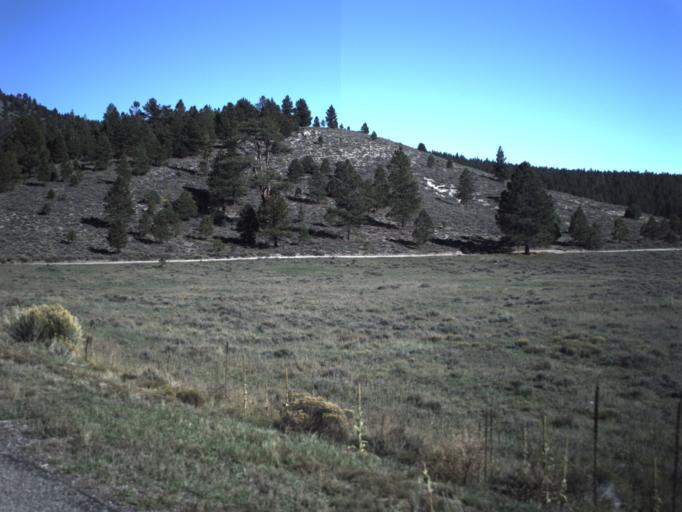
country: US
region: Utah
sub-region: Garfield County
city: Panguitch
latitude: 37.7073
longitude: -112.6296
